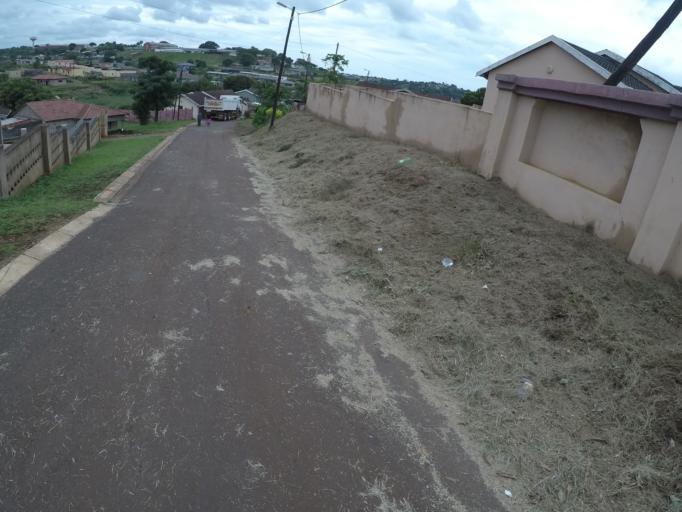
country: ZA
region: KwaZulu-Natal
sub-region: uThungulu District Municipality
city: Empangeni
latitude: -28.7807
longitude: 31.8590
